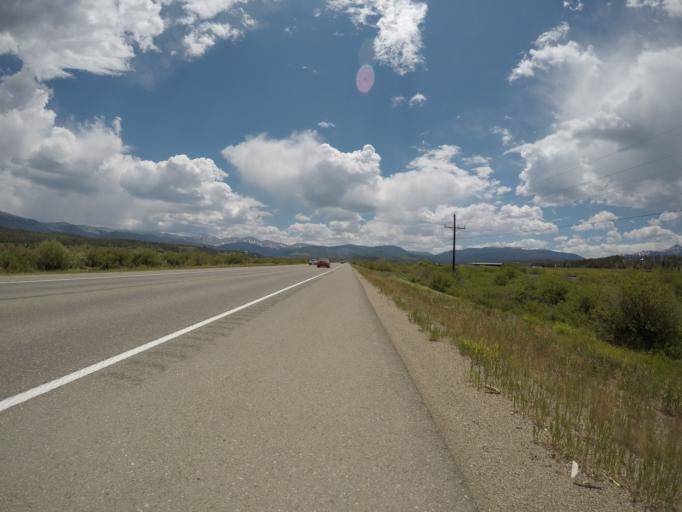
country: US
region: Colorado
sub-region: Grand County
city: Fraser
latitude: 39.9642
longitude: -105.8228
